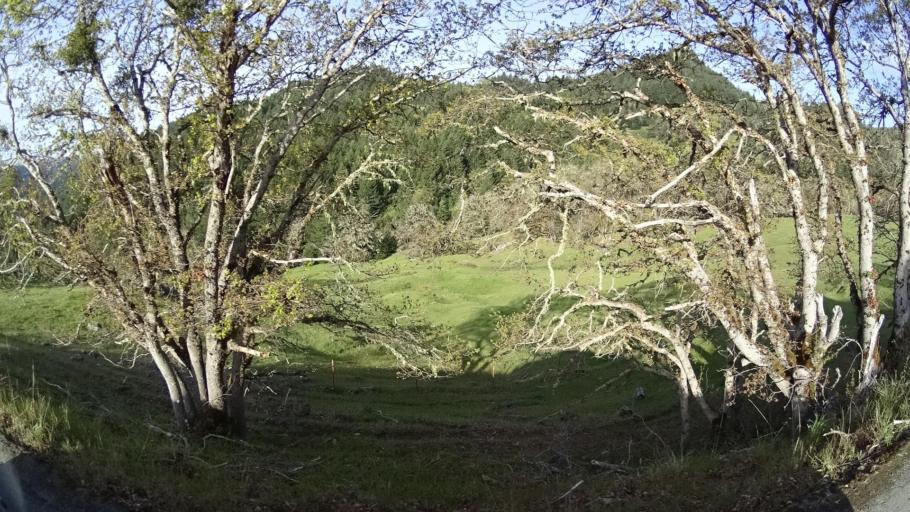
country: US
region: California
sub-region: Humboldt County
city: Blue Lake
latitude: 40.7097
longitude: -123.9394
